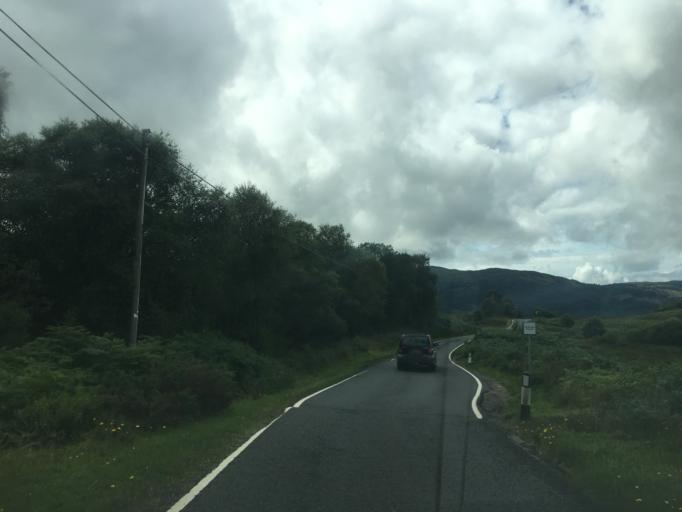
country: GB
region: Scotland
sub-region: Argyll and Bute
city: Port Bannatyne
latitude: 55.9882
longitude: -5.1558
